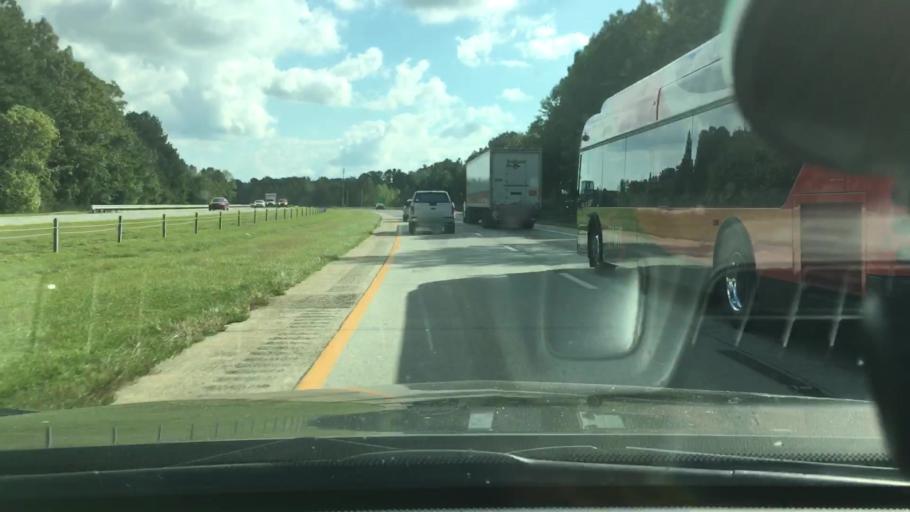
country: US
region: North Carolina
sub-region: Orange County
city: Chapel Hill
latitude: 35.9902
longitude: -79.0757
